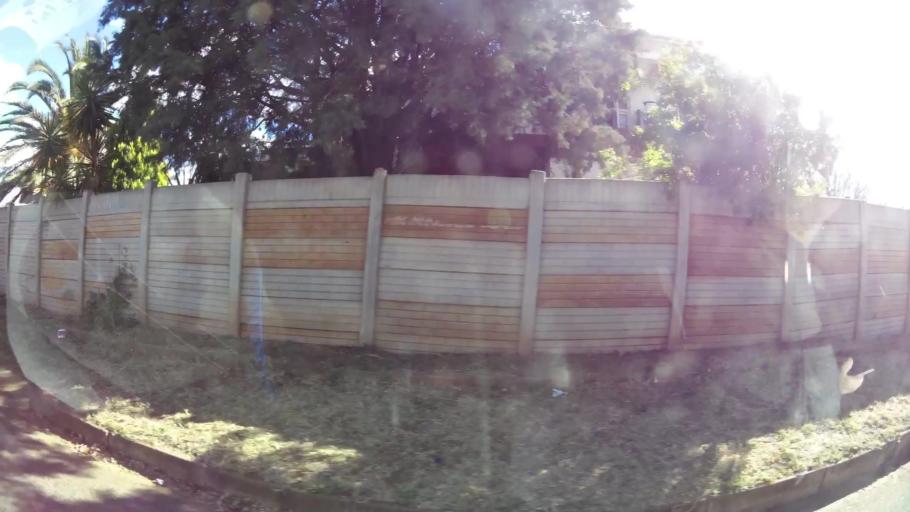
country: ZA
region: North-West
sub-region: Dr Kenneth Kaunda District Municipality
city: Klerksdorp
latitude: -26.8579
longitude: 26.6545
